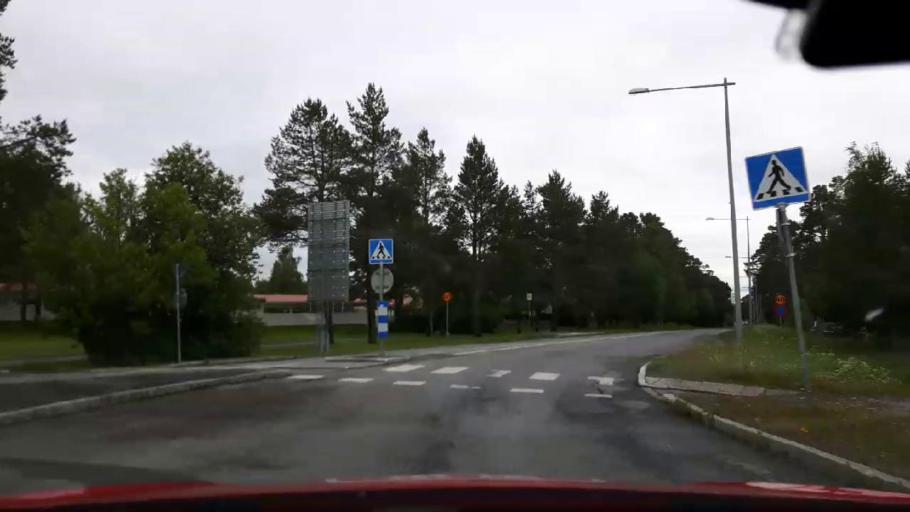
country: SE
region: Jaemtland
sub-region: OEstersunds Kommun
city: Ostersund
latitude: 63.1873
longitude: 14.6509
